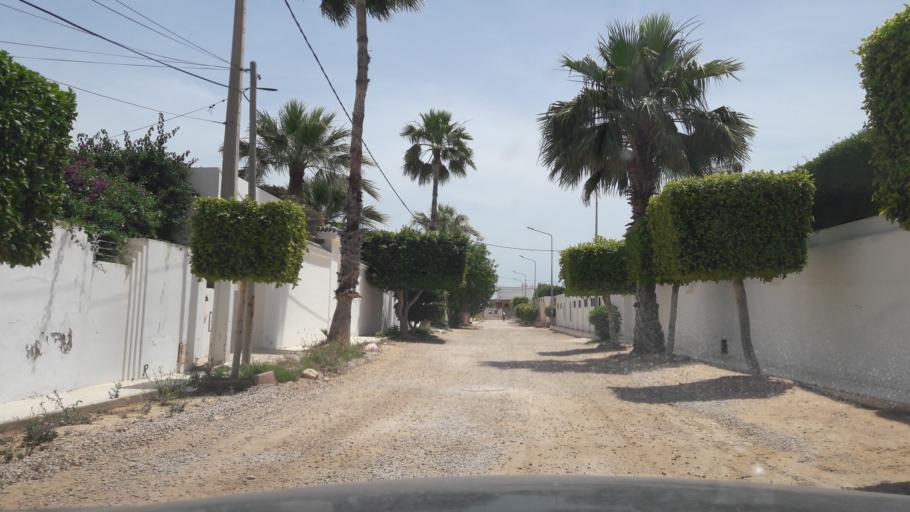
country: TN
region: Safaqis
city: Sfax
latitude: 34.7787
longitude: 10.7568
